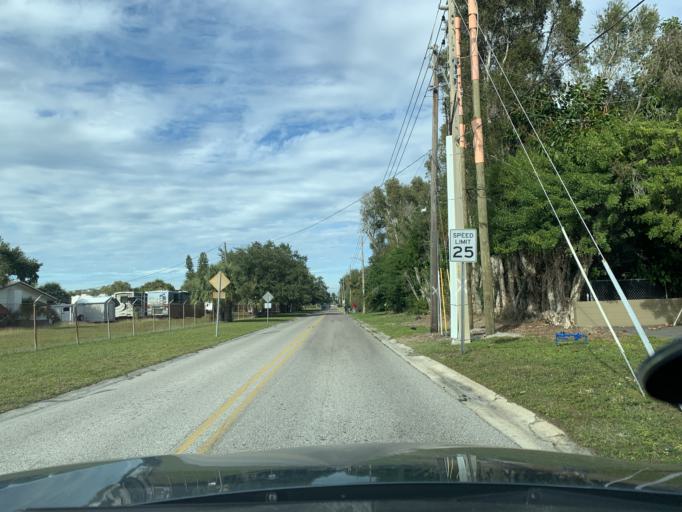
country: US
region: Florida
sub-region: Pinellas County
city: Kenneth City
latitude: 27.7994
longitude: -82.7368
